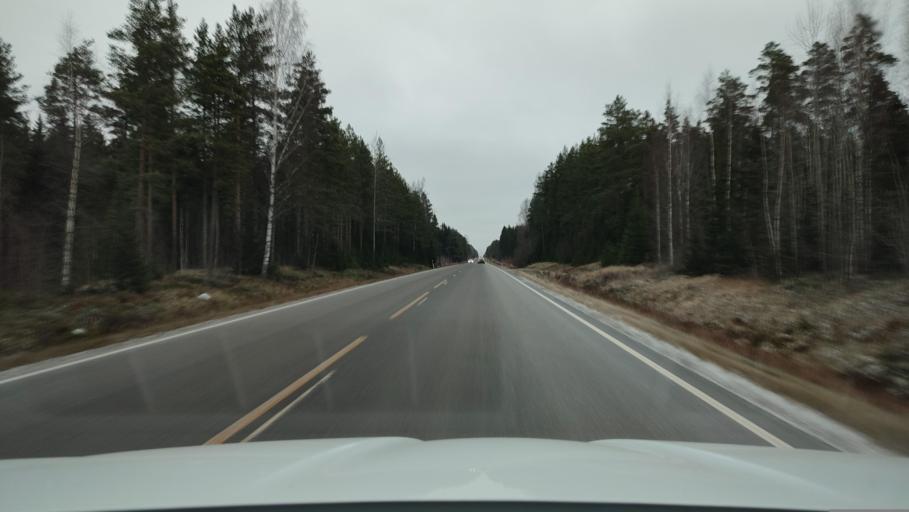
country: FI
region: Ostrobothnia
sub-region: Sydosterbotten
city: Naerpes
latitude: 62.5544
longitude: 21.4752
